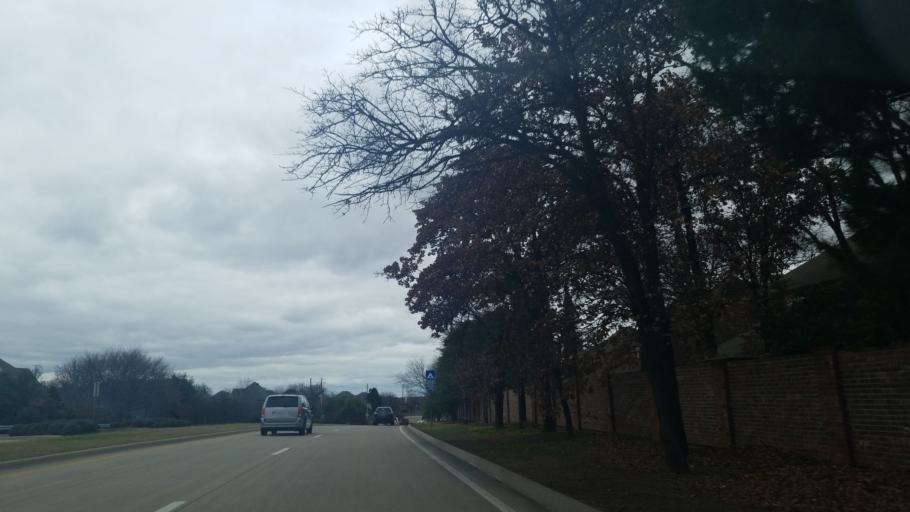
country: US
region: Texas
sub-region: Denton County
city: Copper Canyon
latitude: 33.0966
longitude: -97.0804
